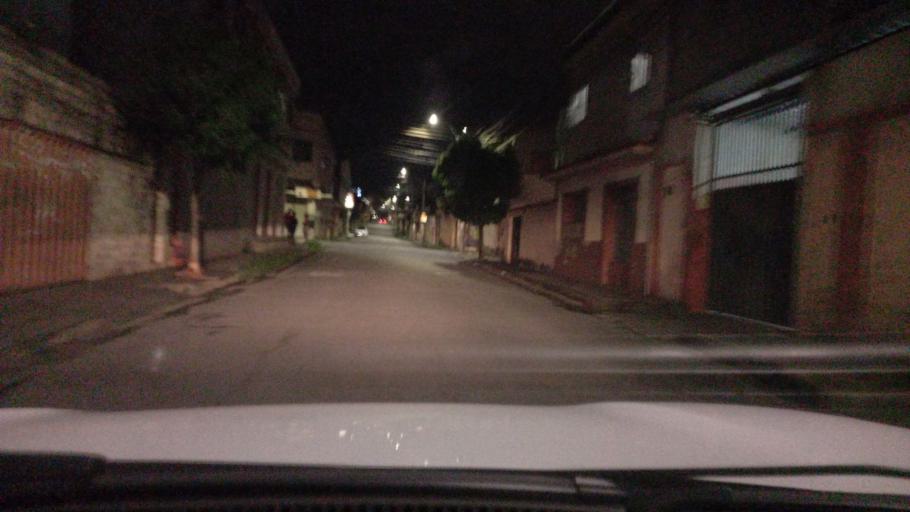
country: BR
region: Minas Gerais
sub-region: Belo Horizonte
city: Belo Horizonte
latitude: -19.8960
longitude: -43.9577
